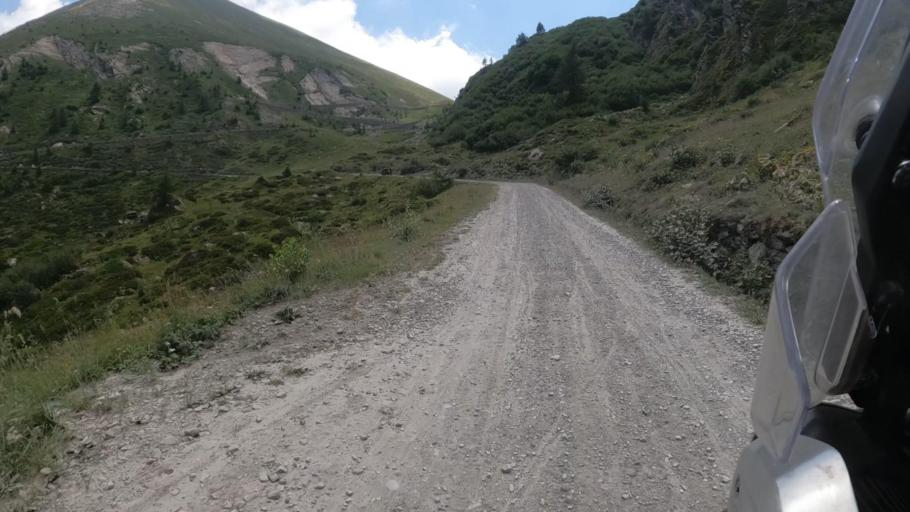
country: IT
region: Piedmont
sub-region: Provincia di Torino
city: Usseaux
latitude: 45.0748
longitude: 7.0522
